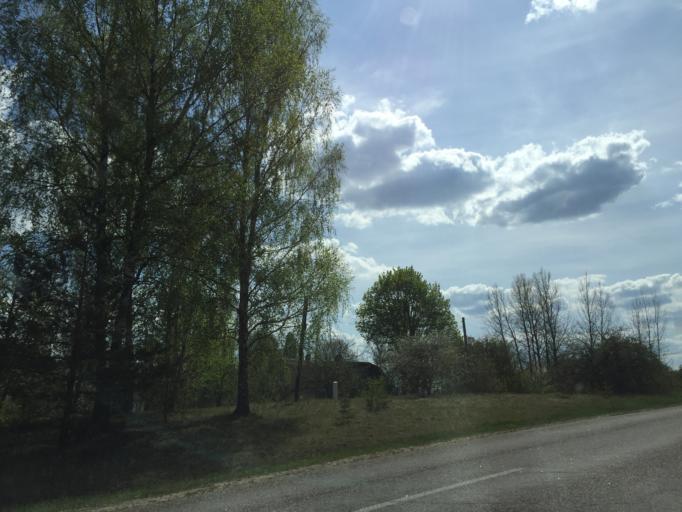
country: LV
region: Limbazu Rajons
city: Limbazi
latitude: 57.3516
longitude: 24.6655
